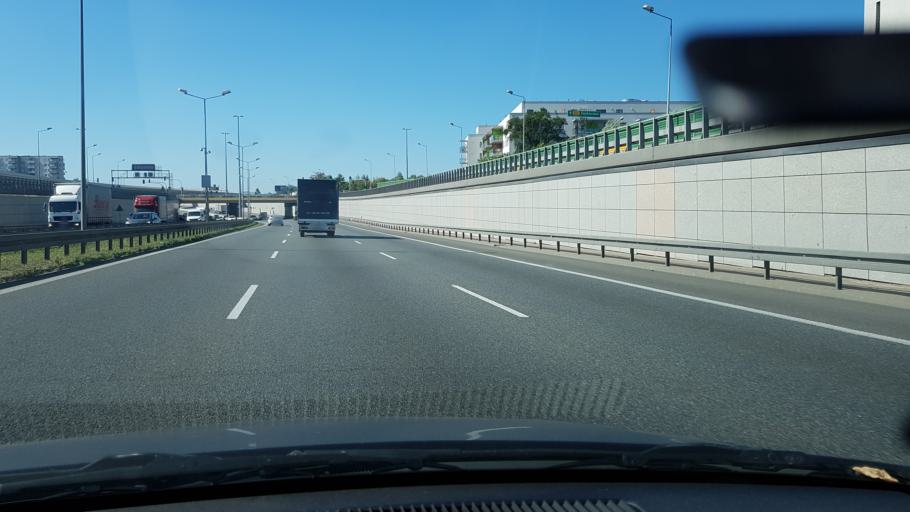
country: PL
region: Masovian Voivodeship
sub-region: Warszawa
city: Bemowo
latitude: 52.2452
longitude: 20.9007
